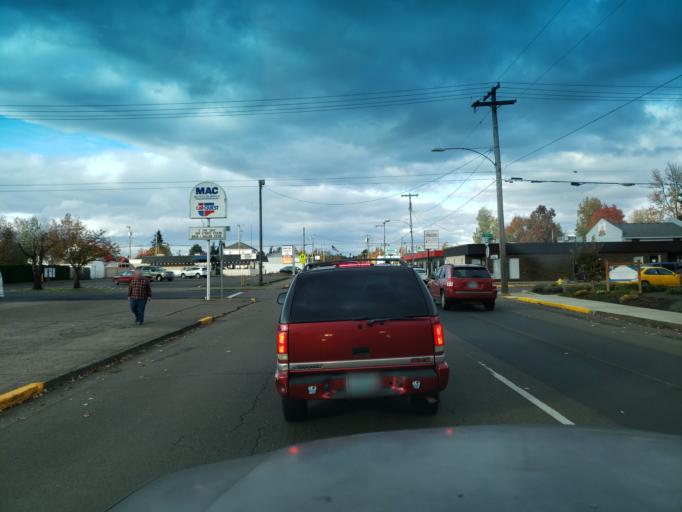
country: US
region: Oregon
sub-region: Yamhill County
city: McMinnville
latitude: 45.2147
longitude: -123.1980
